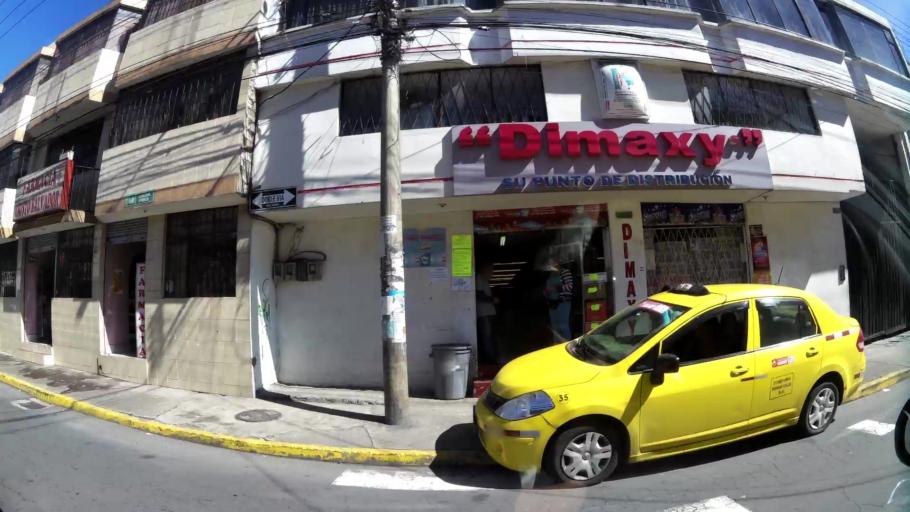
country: EC
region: Pichincha
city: Quito
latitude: -0.2834
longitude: -78.5587
